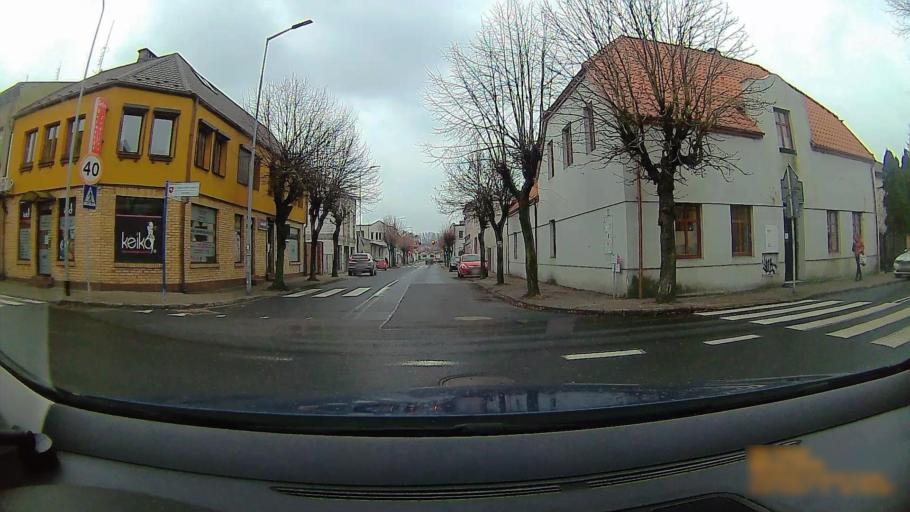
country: PL
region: Greater Poland Voivodeship
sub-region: Konin
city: Konin
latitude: 52.2110
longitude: 18.2511
